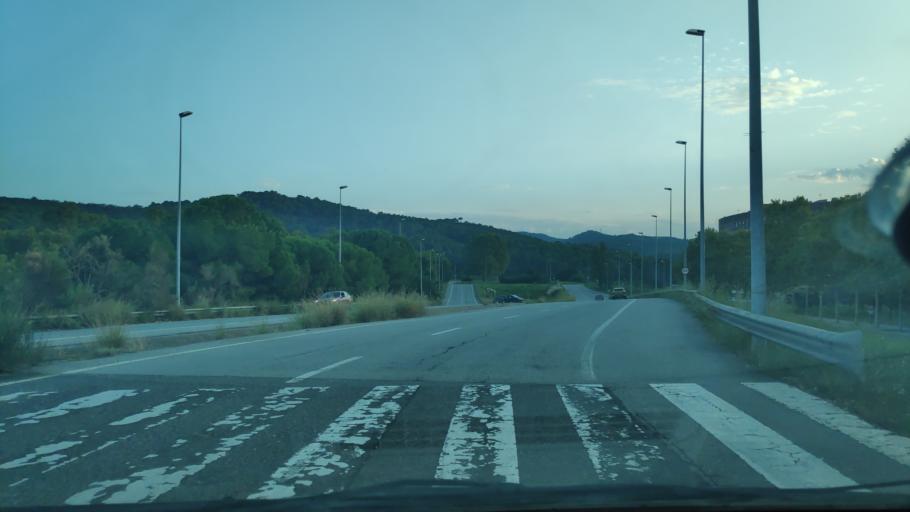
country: ES
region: Catalonia
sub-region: Provincia de Barcelona
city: Ripollet
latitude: 41.4855
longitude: 2.1554
